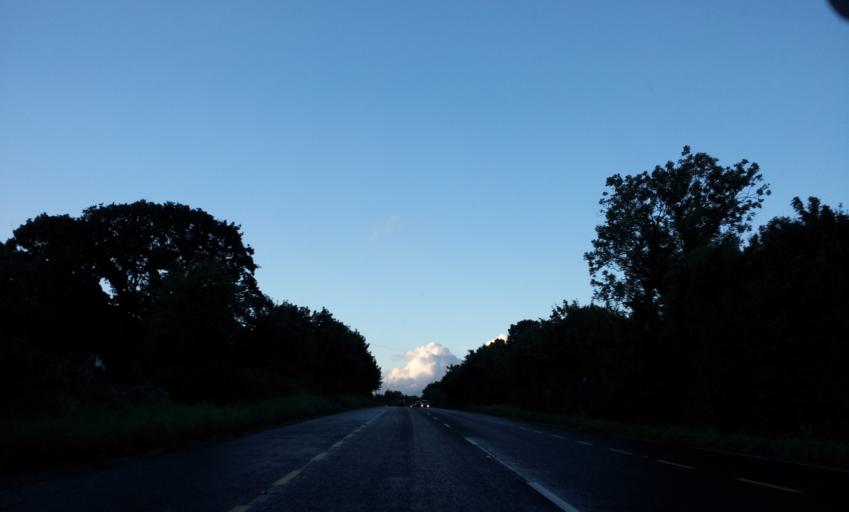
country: IE
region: Munster
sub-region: County Limerick
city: Rathkeale
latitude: 52.5032
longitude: -8.9917
